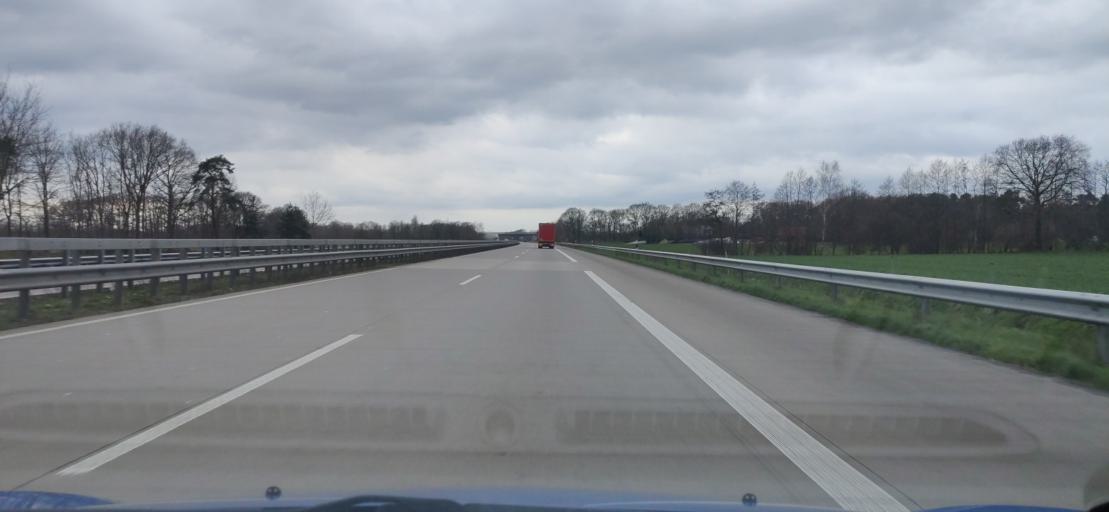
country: DE
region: Lower Saxony
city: Quendorf
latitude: 52.3440
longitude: 7.2056
